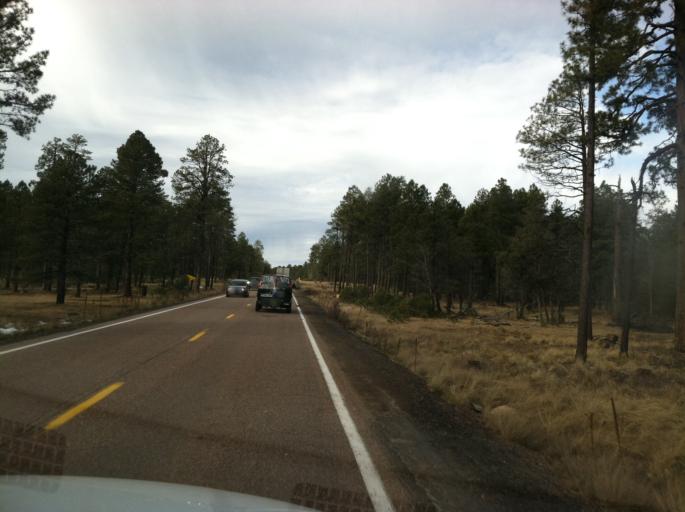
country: US
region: Arizona
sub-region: Navajo County
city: Heber-Overgaard
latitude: 34.2998
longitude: -110.8741
